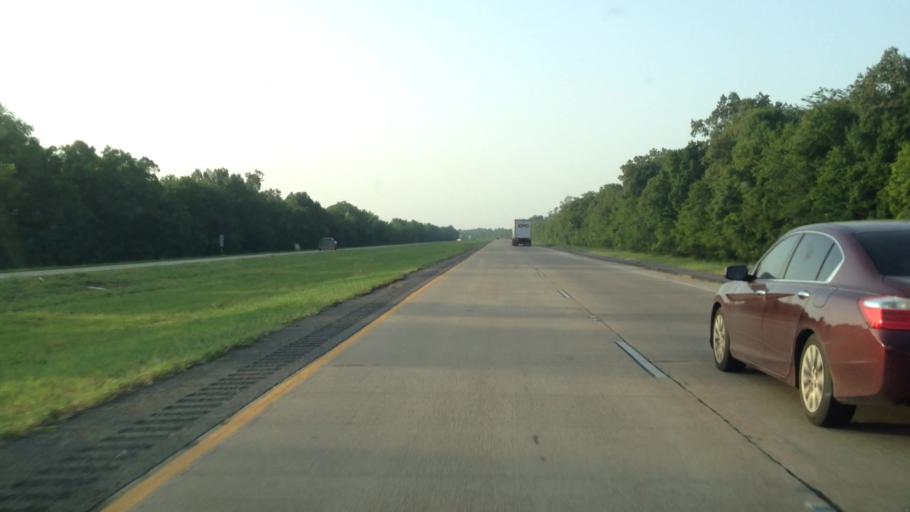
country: US
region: Louisiana
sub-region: Natchitoches Parish
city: Vienna Bend
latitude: 31.5879
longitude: -93.0303
